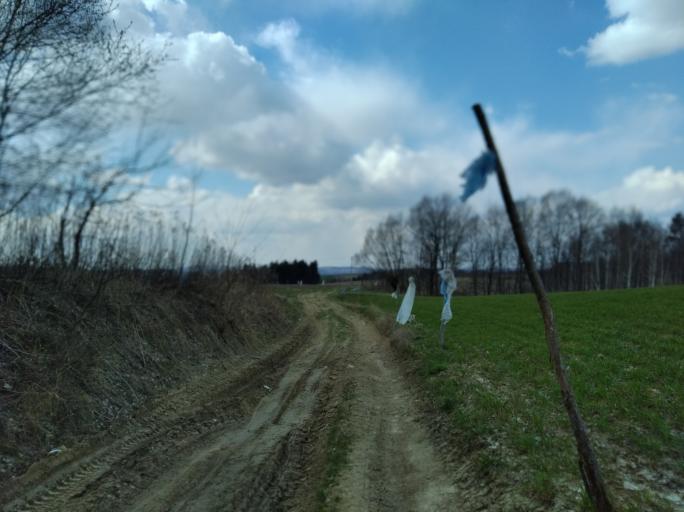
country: PL
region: Subcarpathian Voivodeship
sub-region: Powiat strzyzowski
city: Strzyzow
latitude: 49.9086
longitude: 21.7669
